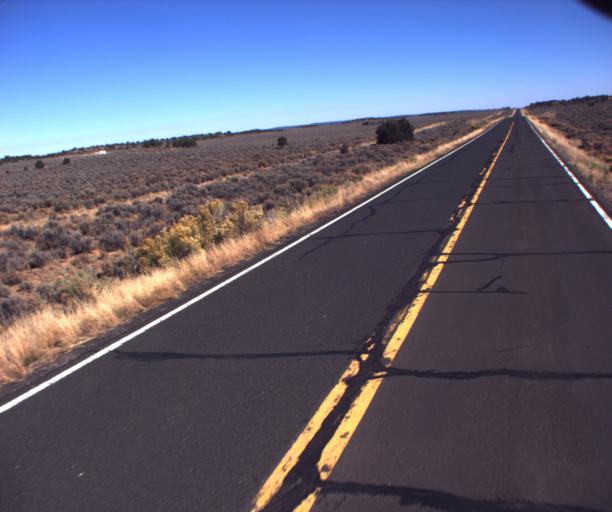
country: US
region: Arizona
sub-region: Navajo County
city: First Mesa
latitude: 35.7418
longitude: -110.0705
